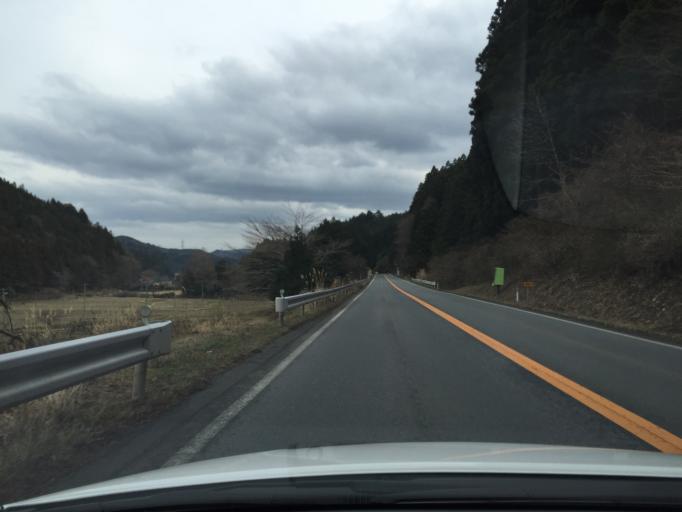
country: JP
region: Fukushima
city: Ishikawa
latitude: 37.1466
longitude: 140.6708
